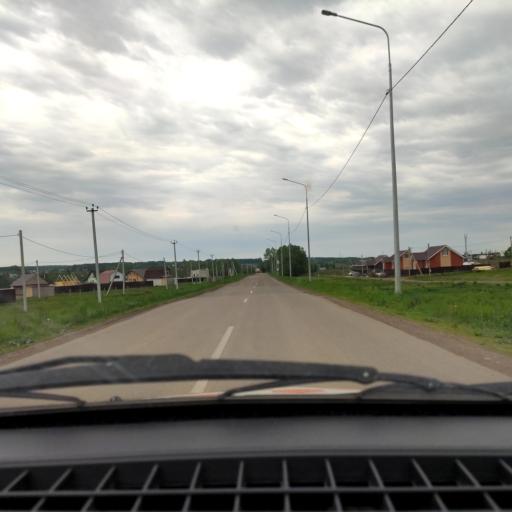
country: RU
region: Bashkortostan
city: Avdon
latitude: 54.5544
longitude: 55.7582
